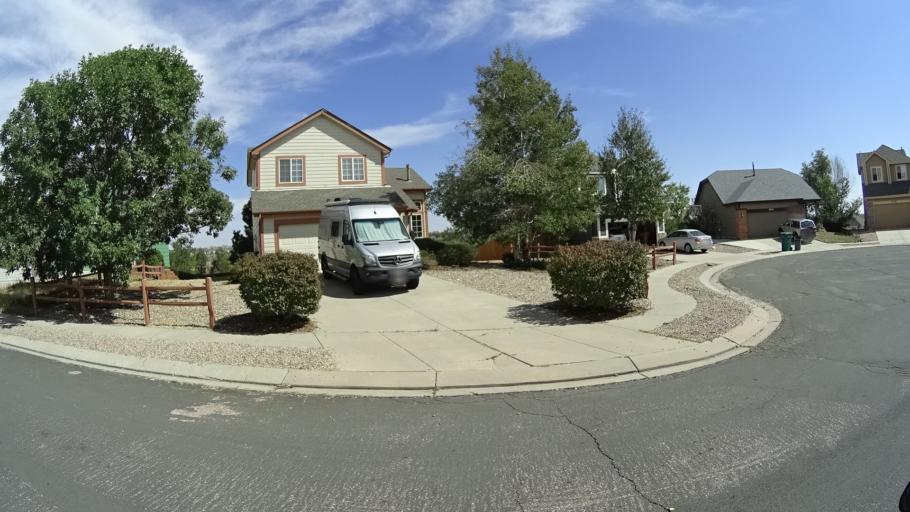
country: US
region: Colorado
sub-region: El Paso County
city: Cimarron Hills
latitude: 38.8995
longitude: -104.7141
